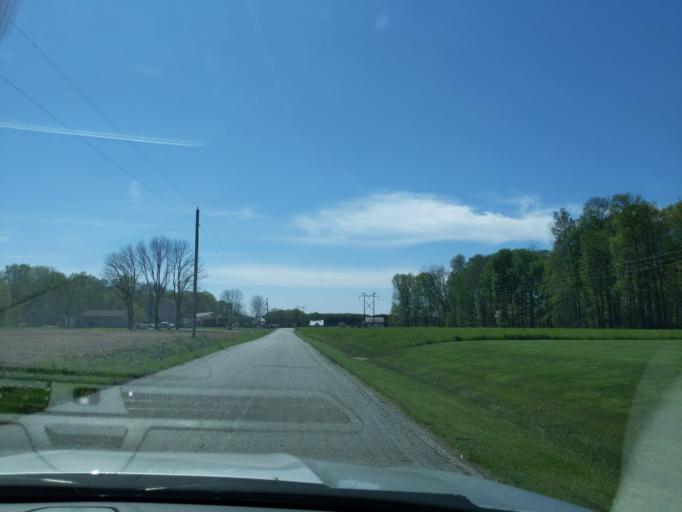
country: US
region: Indiana
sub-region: Decatur County
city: Greensburg
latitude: 39.2337
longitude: -85.4308
